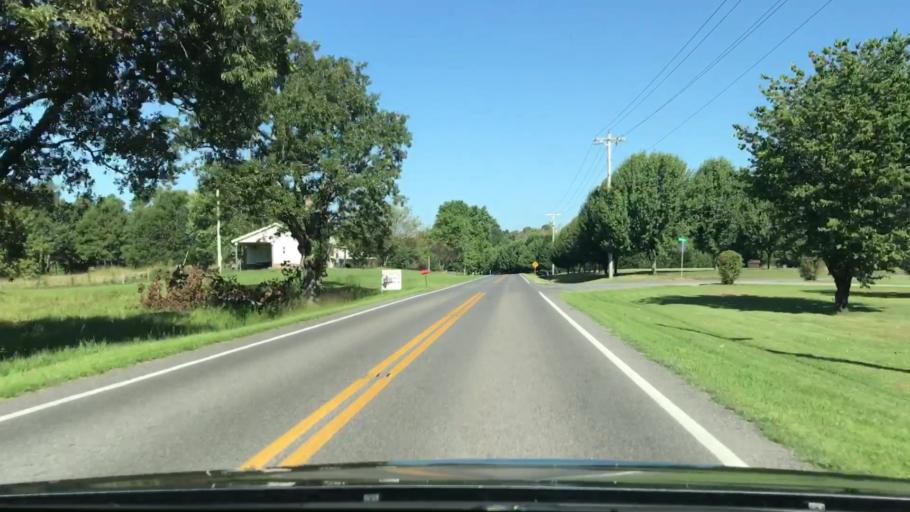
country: US
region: Kentucky
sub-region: Graves County
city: Mayfield
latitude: 36.7775
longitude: -88.5098
